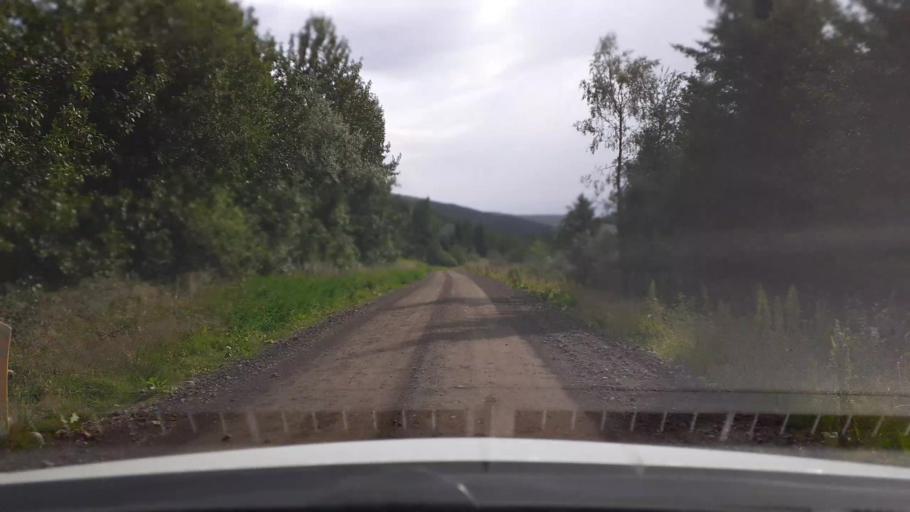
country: IS
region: Capital Region
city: Mosfellsbaer
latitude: 64.5206
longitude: -21.4413
